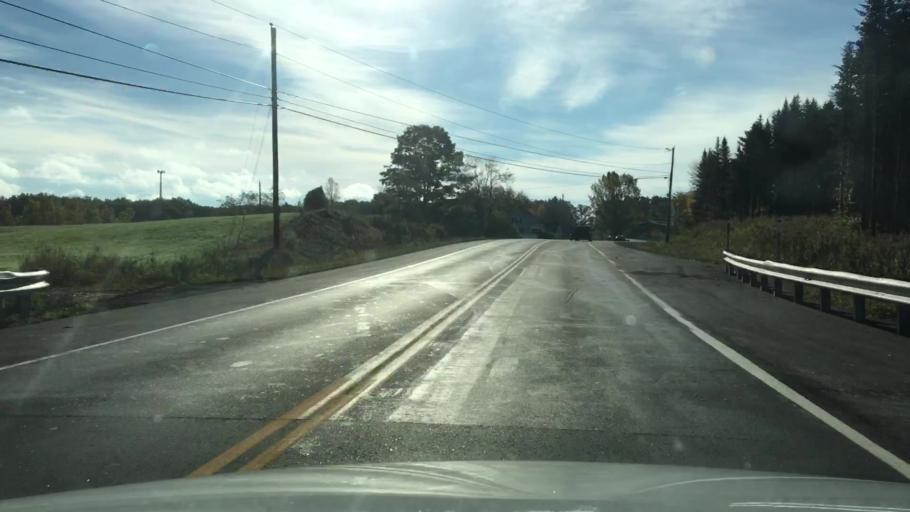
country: US
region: Maine
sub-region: Knox County
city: Warren
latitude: 44.0965
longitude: -69.2429
